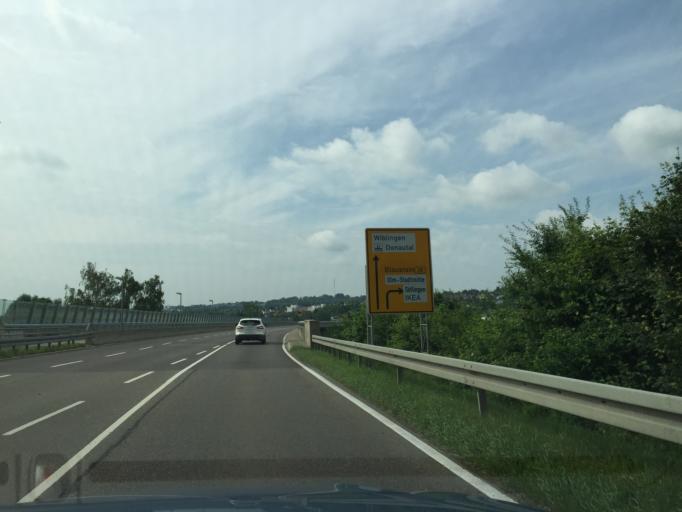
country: DE
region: Baden-Wuerttemberg
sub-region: Tuebingen Region
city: Ulm
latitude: 48.4064
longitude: 9.9475
